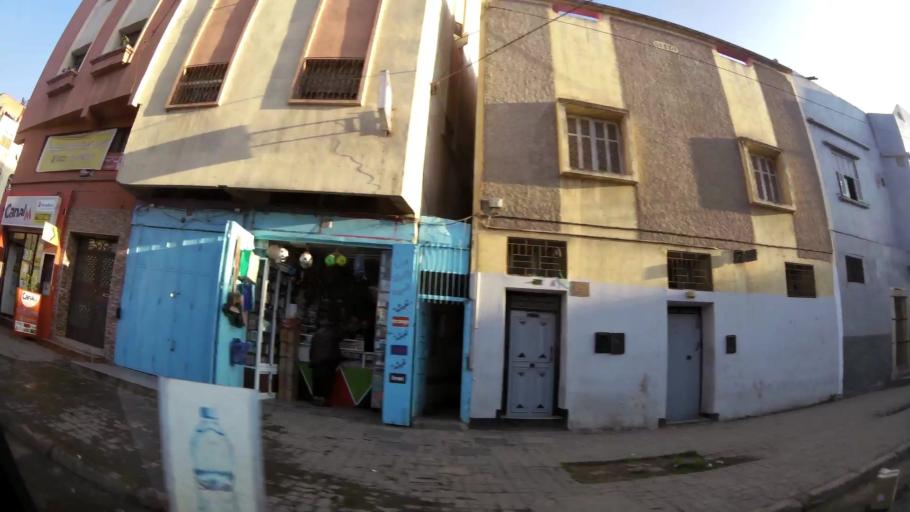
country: MA
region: Chaouia-Ouardigha
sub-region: Settat Province
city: Settat
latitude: 33.0006
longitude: -7.6162
